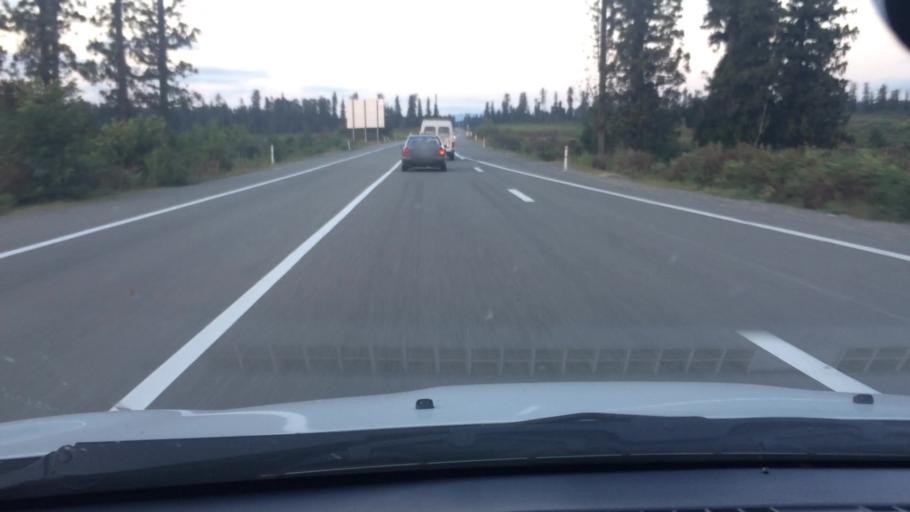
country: GE
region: Ajaria
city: Ochkhamuri
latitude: 41.8348
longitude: 41.8235
